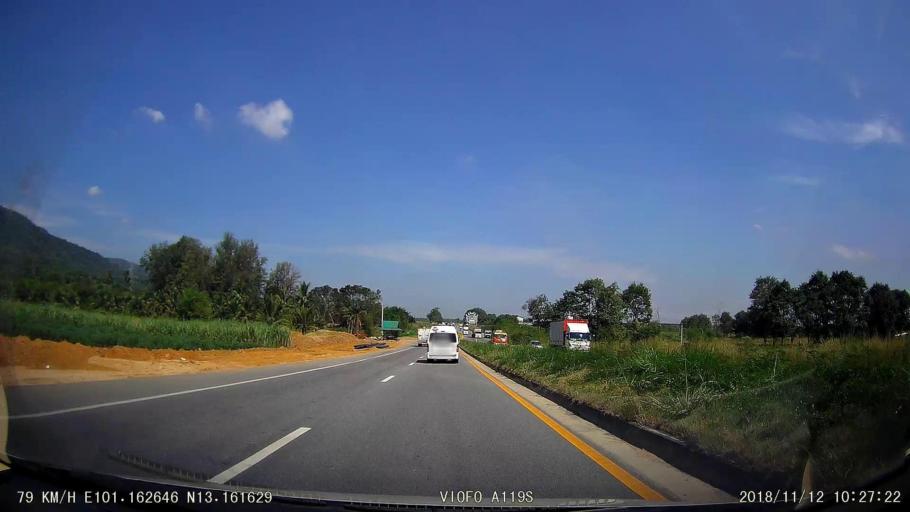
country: TH
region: Chon Buri
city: Ban Bueng
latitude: 13.1553
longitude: 101.1632
